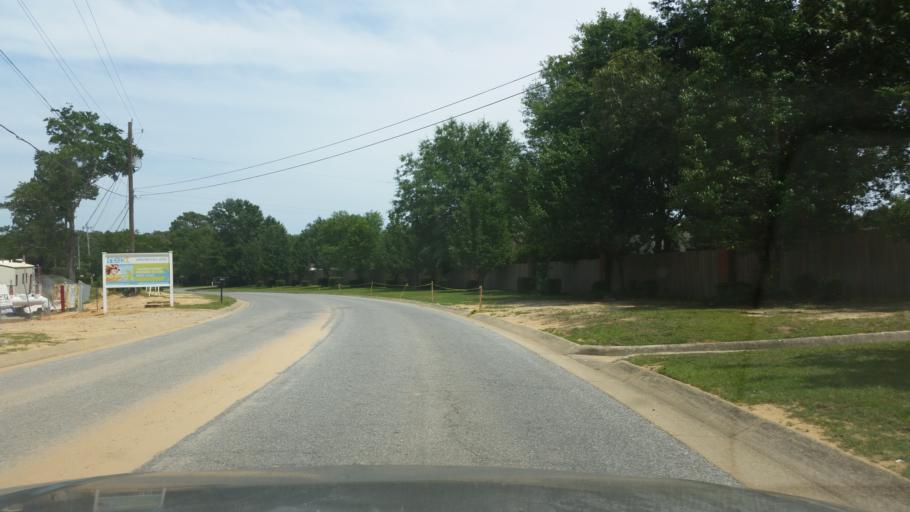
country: US
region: Florida
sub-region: Escambia County
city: Ferry Pass
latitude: 30.5397
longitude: -87.2154
